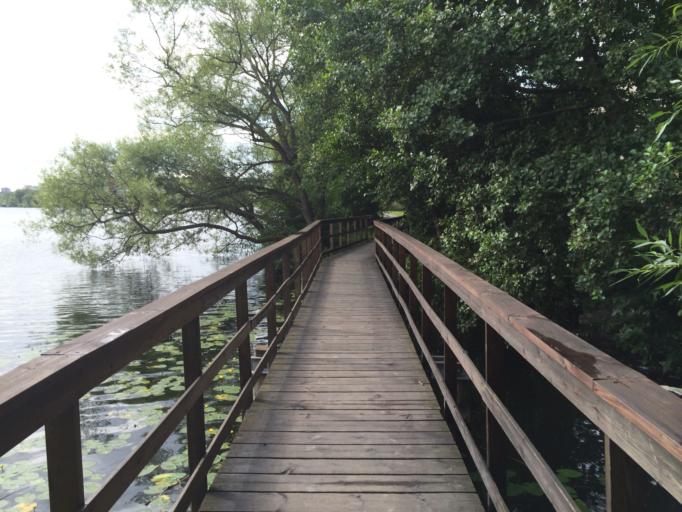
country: SE
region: Stockholm
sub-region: Solna Kommun
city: Solna
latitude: 59.3312
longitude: 17.9852
